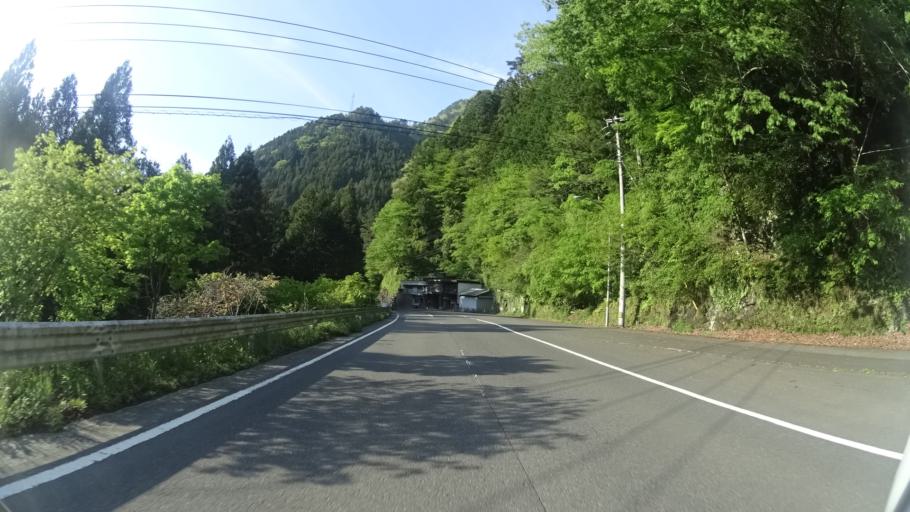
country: JP
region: Tokushima
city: Ikedacho
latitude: 33.8689
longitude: 133.8727
